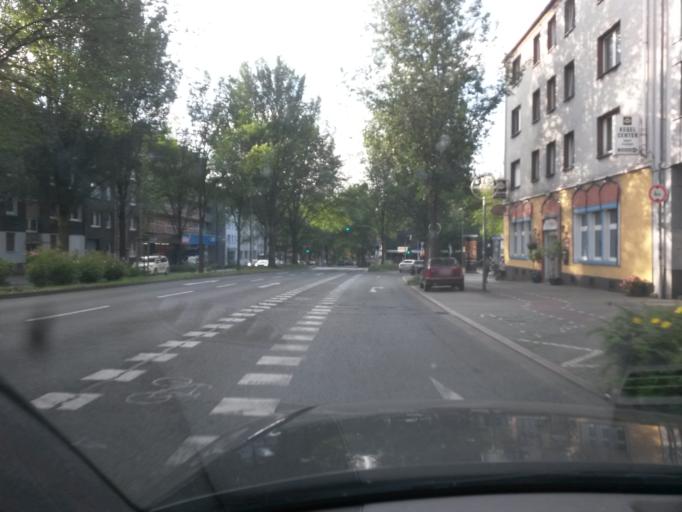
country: DE
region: North Rhine-Westphalia
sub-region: Regierungsbezirk Arnsberg
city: Dortmund
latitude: 51.5047
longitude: 7.4760
